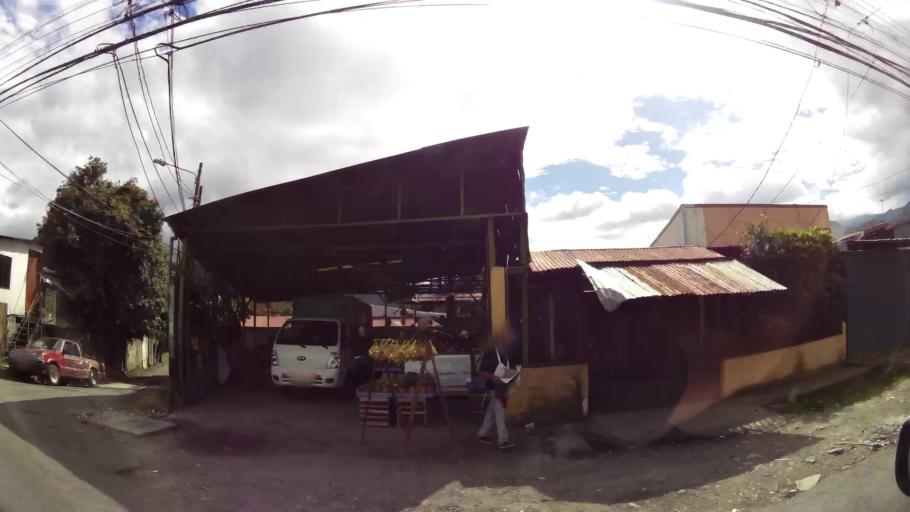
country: CR
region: San Jose
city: San Rafael Arriba
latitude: 9.8772
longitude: -84.0794
